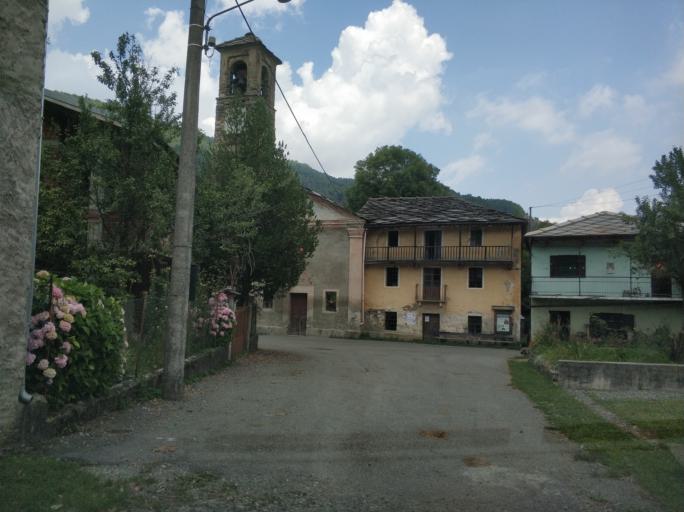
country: IT
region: Piedmont
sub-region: Provincia di Torino
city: Viu
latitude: 45.2144
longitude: 7.3940
